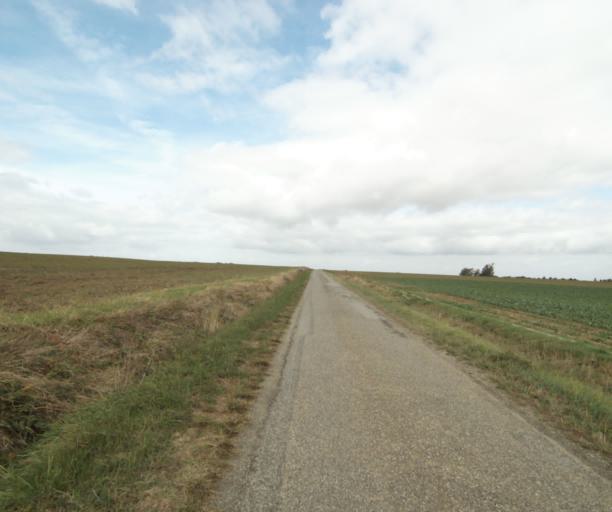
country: FR
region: Midi-Pyrenees
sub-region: Departement du Tarn-et-Garonne
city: Beaumont-de-Lomagne
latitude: 43.8683
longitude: 1.0890
